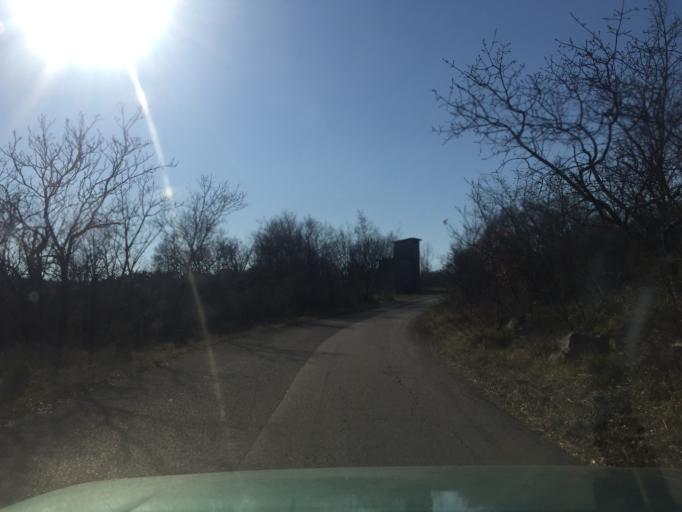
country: IT
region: Friuli Venezia Giulia
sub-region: Provincia di Gorizia
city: Doberdo del Lago
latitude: 45.8558
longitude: 13.5637
